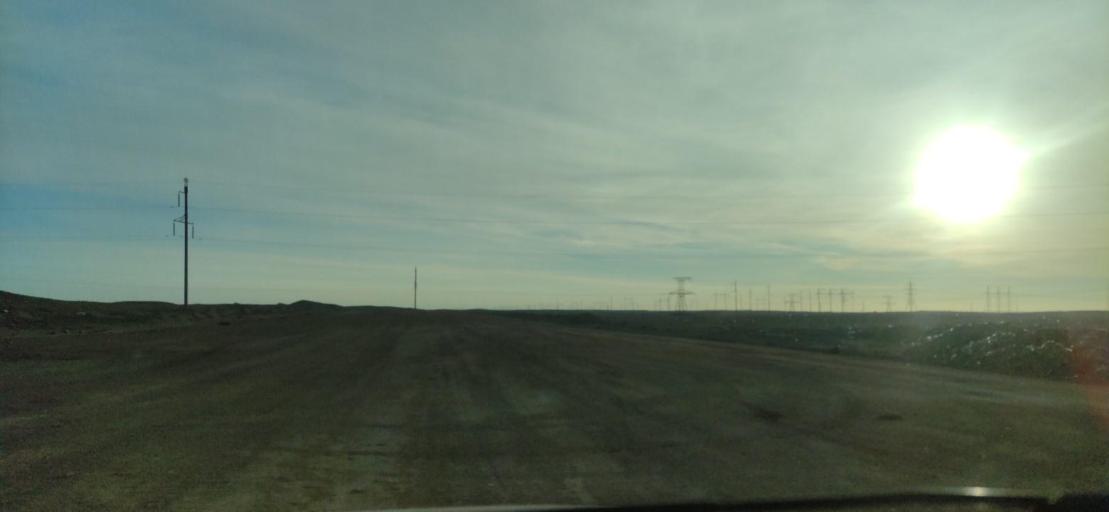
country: KZ
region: Qaraghandy
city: Saryshaghan
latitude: 46.1239
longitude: 73.5958
